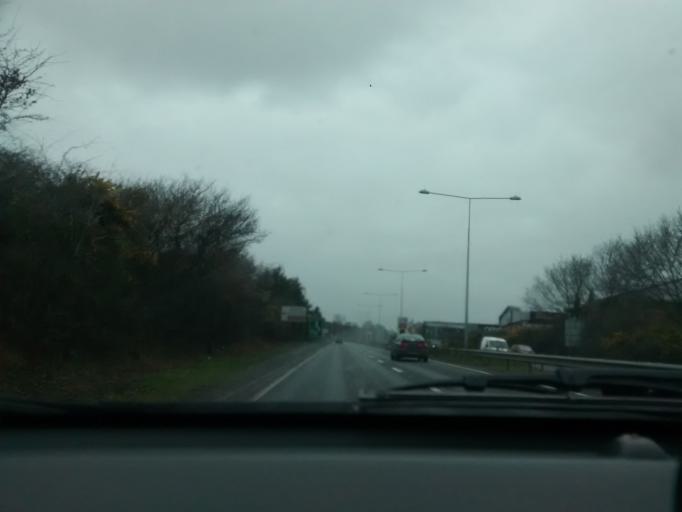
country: GB
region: England
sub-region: Suffolk
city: Kesgrave
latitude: 52.0629
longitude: 1.2756
